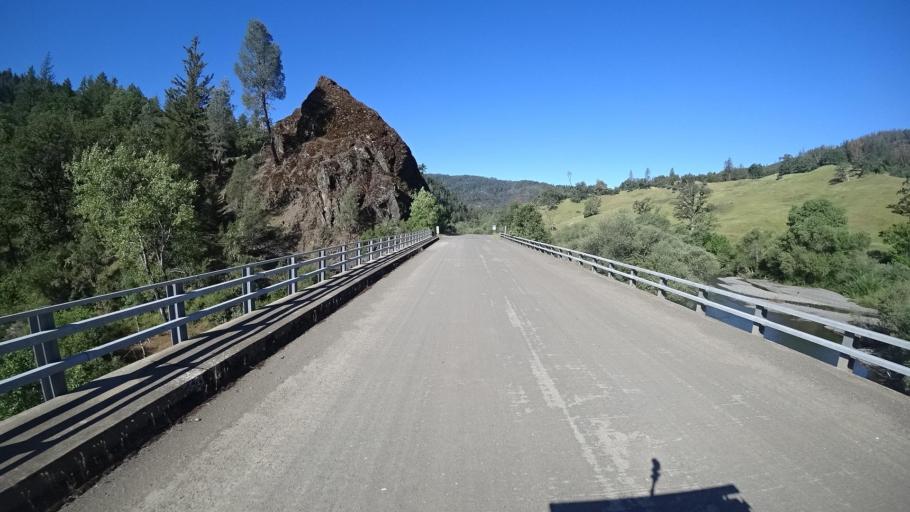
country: US
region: California
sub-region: Lake County
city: Upper Lake
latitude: 39.4102
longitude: -122.9793
